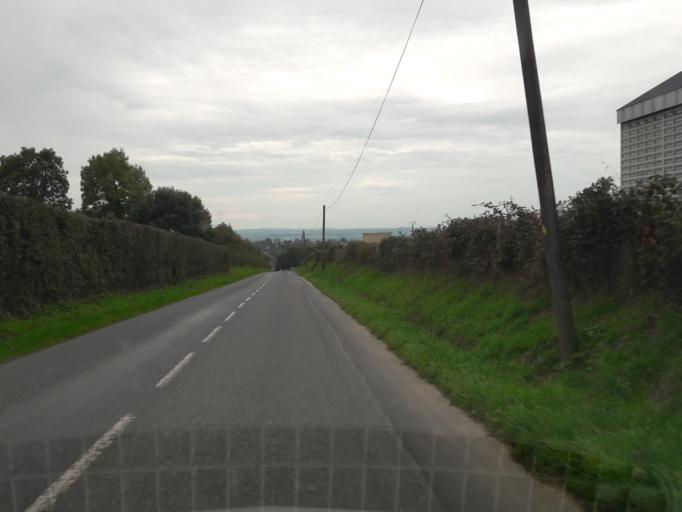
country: FR
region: Lower Normandy
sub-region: Departement du Calvados
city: Cahagnes
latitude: 49.0875
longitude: -0.8074
